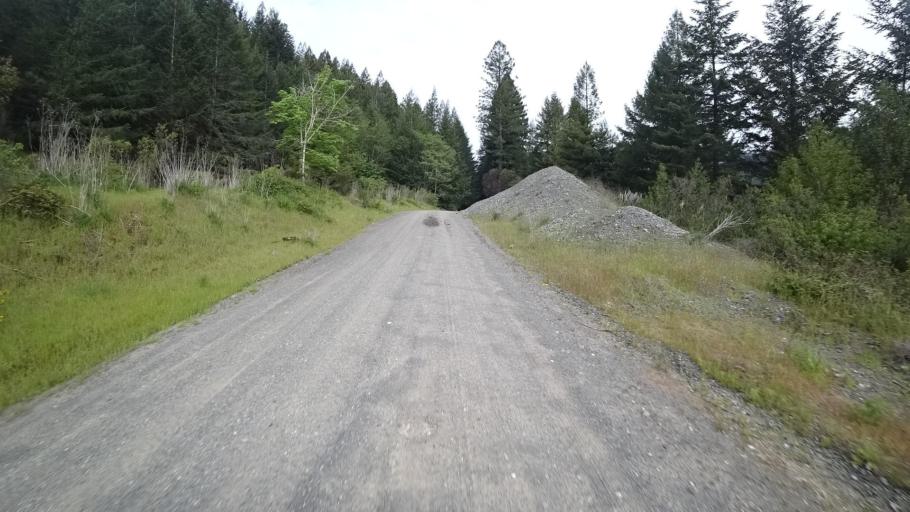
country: US
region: California
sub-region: Humboldt County
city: Redway
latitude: 40.3241
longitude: -123.8369
